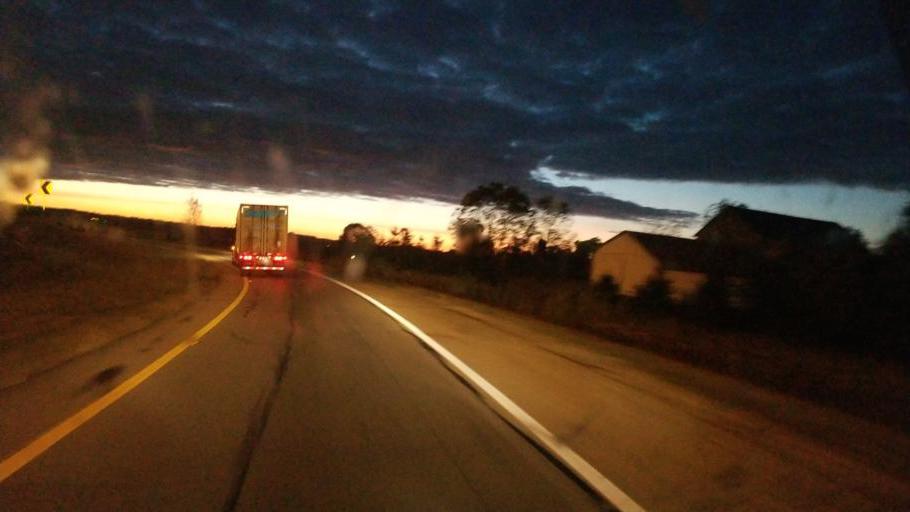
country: US
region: Ohio
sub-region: Medina County
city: Westfield Center
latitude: 41.0262
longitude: -81.8972
